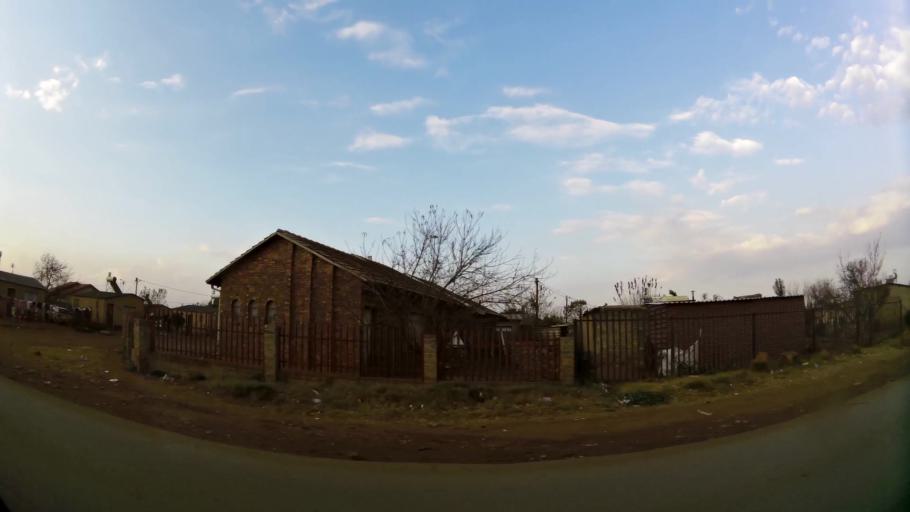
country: ZA
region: Gauteng
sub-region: City of Johannesburg Metropolitan Municipality
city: Orange Farm
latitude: -26.5594
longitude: 27.8318
